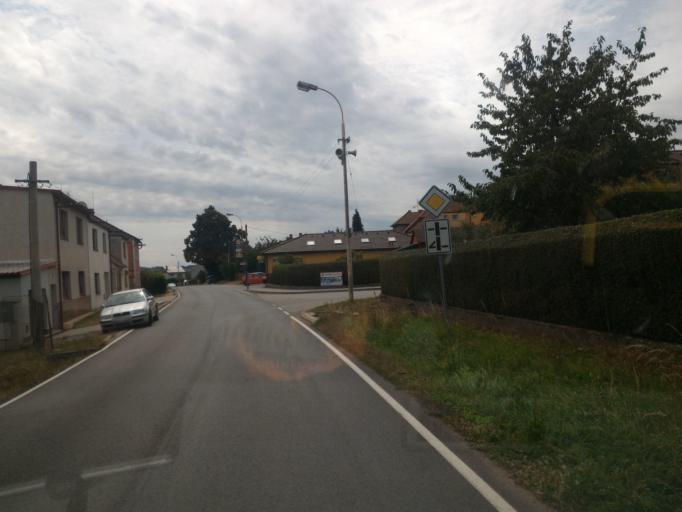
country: CZ
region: Jihocesky
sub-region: Okres Jindrichuv Hradec
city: Dacice
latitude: 49.0866
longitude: 15.4283
